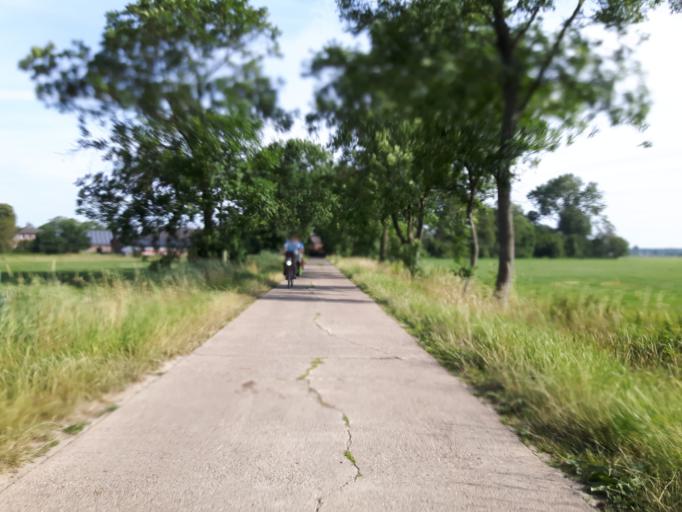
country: DE
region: Lower Saxony
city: Neuenkirchen
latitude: 53.1718
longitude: 8.5081
